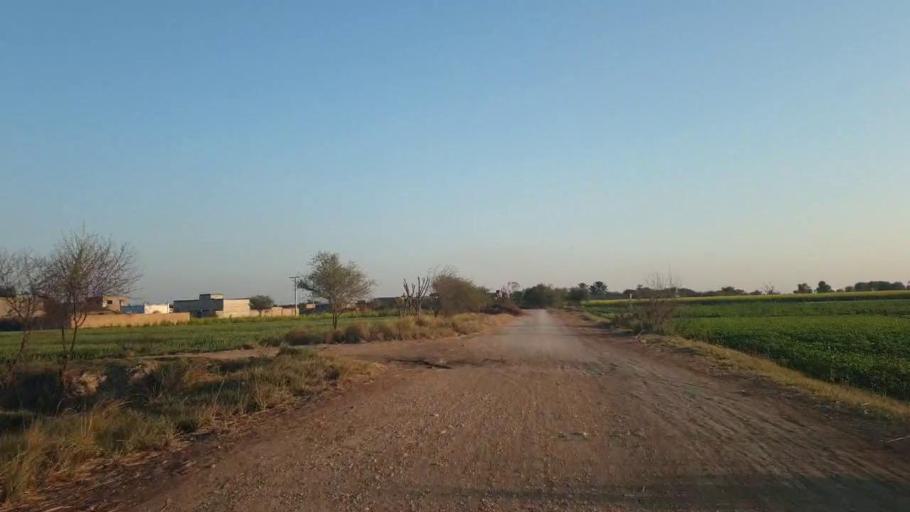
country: PK
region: Sindh
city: Khadro
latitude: 26.0750
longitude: 68.6896
